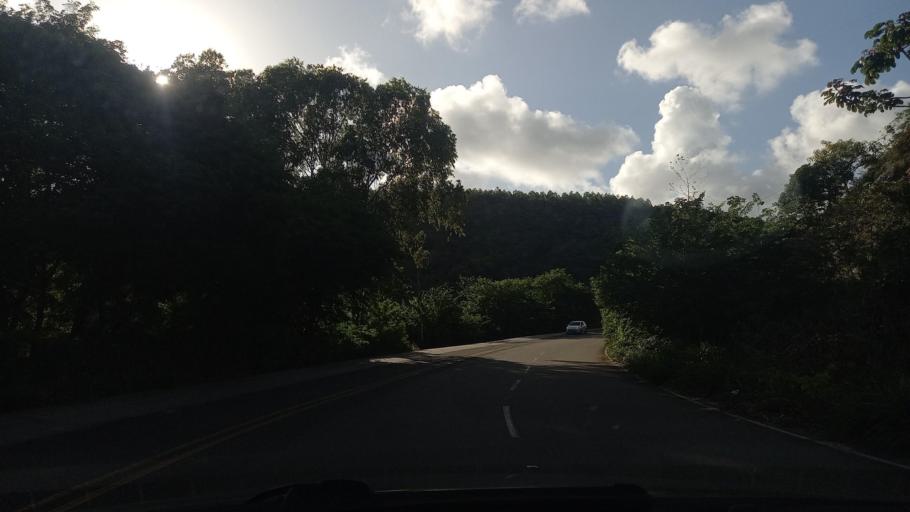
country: BR
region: Alagoas
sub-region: Marechal Deodoro
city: Marechal Deodoro
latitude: -9.8363
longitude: -35.9288
